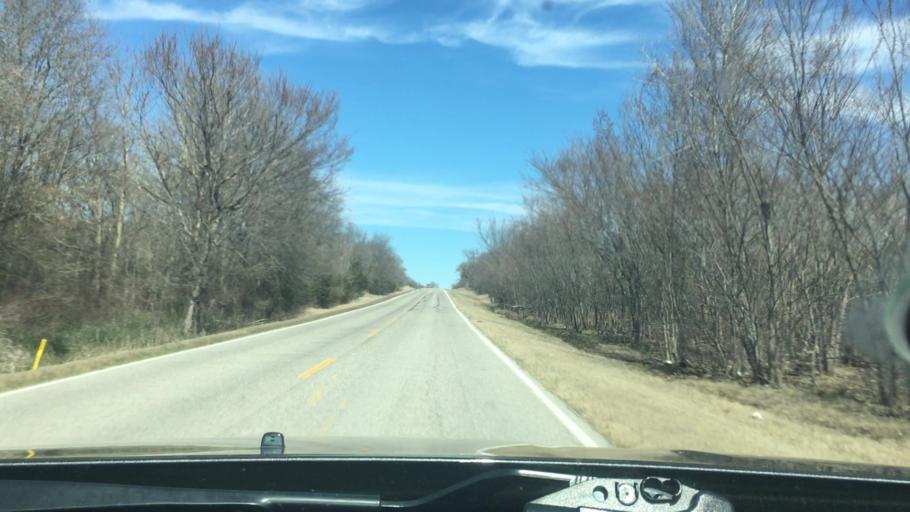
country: US
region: Oklahoma
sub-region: Carter County
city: Dickson
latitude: 34.3144
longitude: -96.9620
